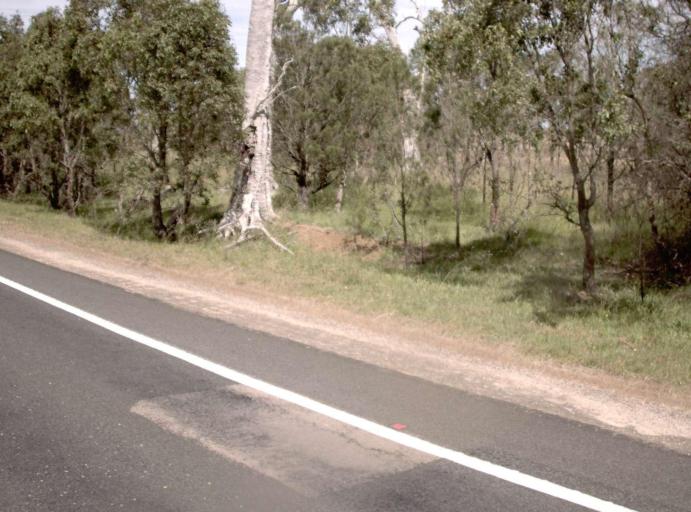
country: AU
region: Victoria
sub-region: East Gippsland
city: Bairnsdale
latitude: -37.8621
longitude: 147.5078
